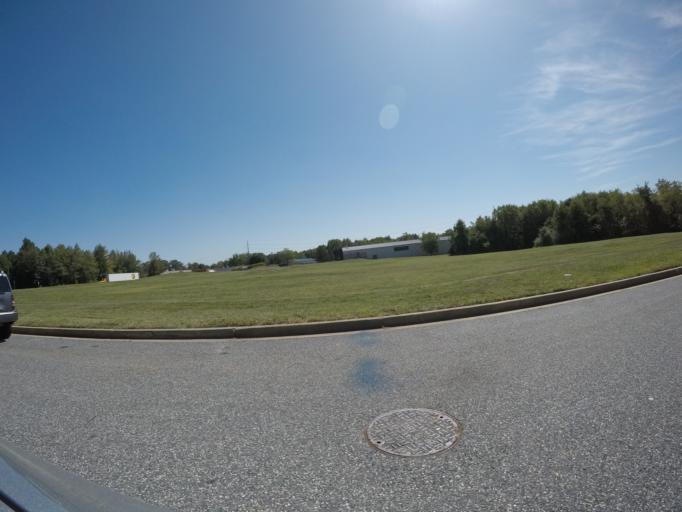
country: US
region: Maryland
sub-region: Harford County
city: Edgewood
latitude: 39.4478
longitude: -76.2921
